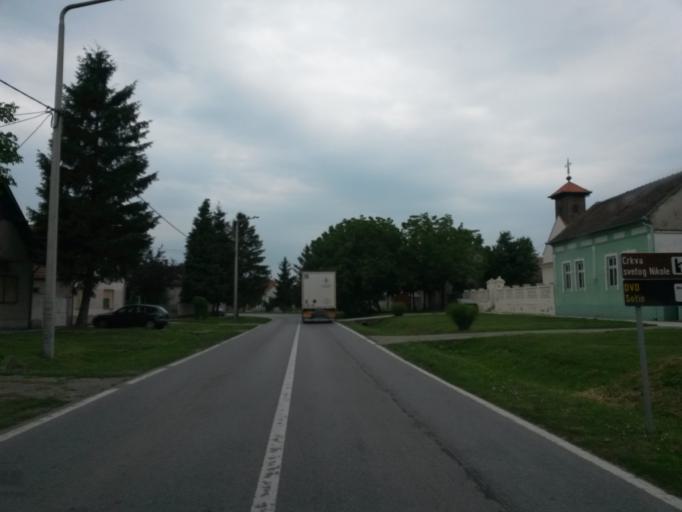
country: HR
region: Vukovarsko-Srijemska
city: Negoslavci
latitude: 45.2982
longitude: 19.0946
